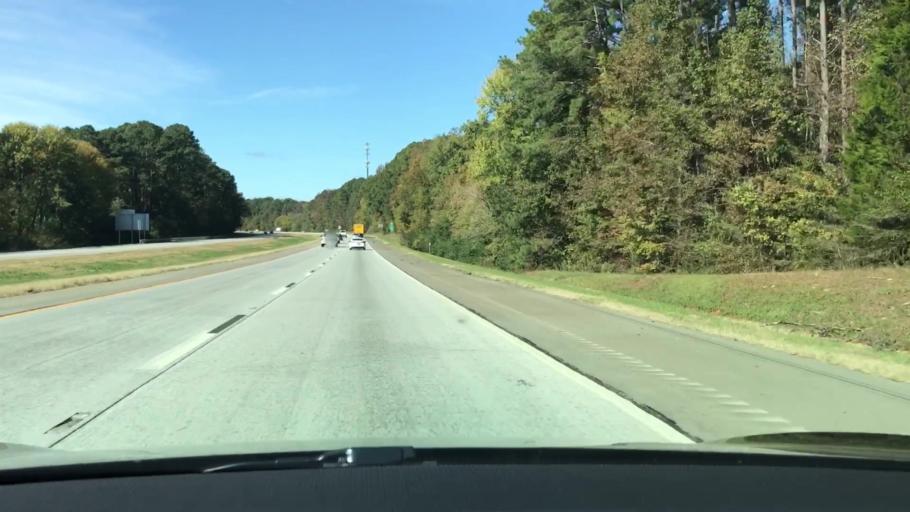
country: US
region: Georgia
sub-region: Morgan County
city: Madison
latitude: 33.5541
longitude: -83.3679
